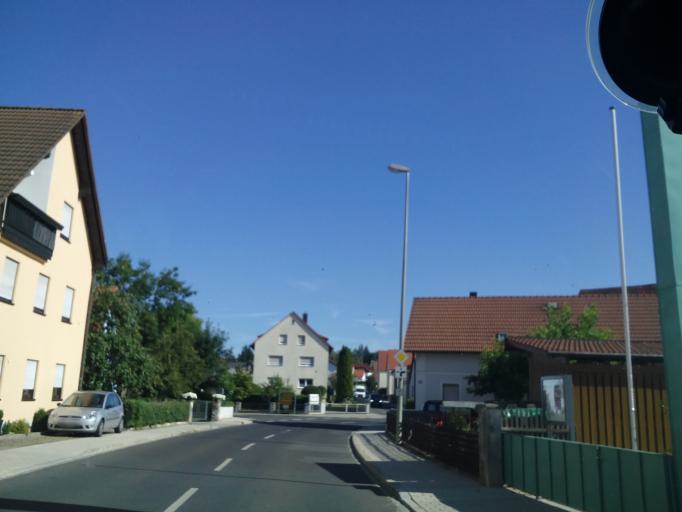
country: DE
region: Bavaria
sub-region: Upper Franconia
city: Buttenheim
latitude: 49.8039
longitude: 11.0339
